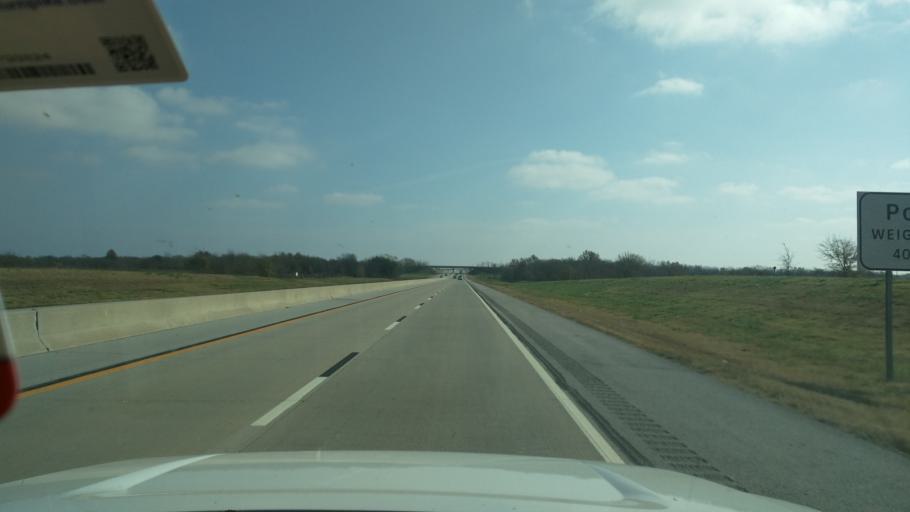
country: US
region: Oklahoma
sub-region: Wagoner County
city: Coweta
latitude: 35.9065
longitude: -95.5344
